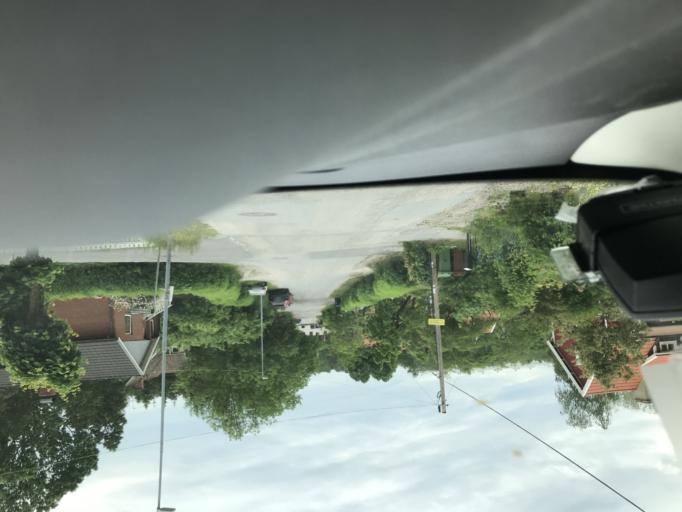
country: SE
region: Stockholm
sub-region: Botkyrka Kommun
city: Tumba
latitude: 59.1945
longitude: 17.8213
